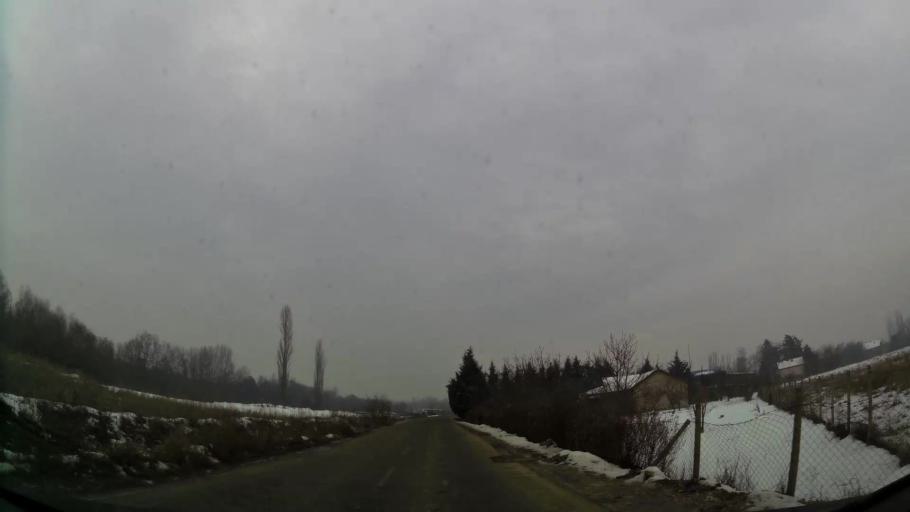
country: MK
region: Cucer-Sandevo
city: Chucher - Sandevo
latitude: 42.0492
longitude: 21.3656
